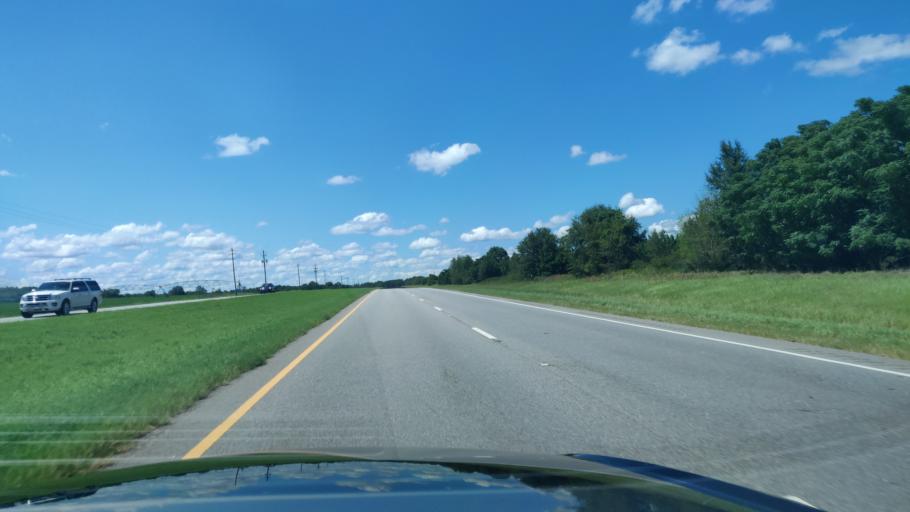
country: US
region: Georgia
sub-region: Terrell County
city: Dawson
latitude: 31.8411
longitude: -84.4697
